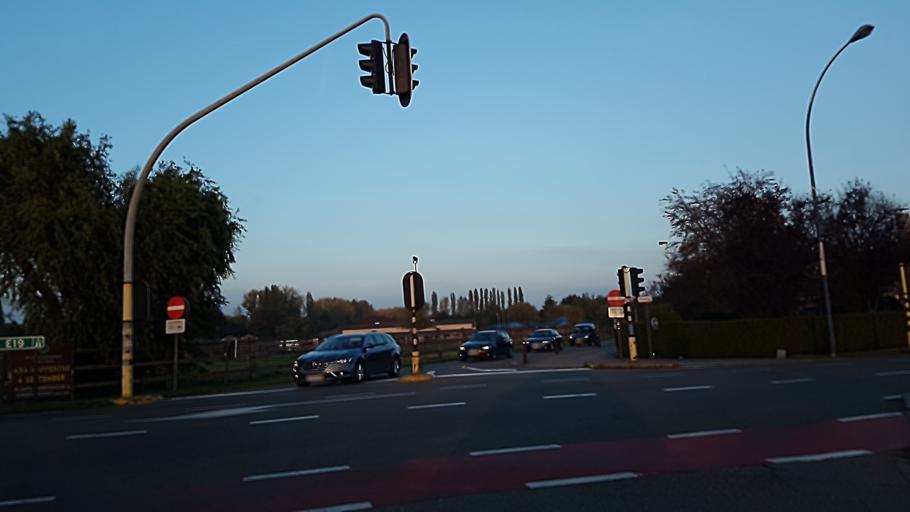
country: BE
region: Flanders
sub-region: Provincie Antwerpen
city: Kontich
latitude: 51.1252
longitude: 4.4592
